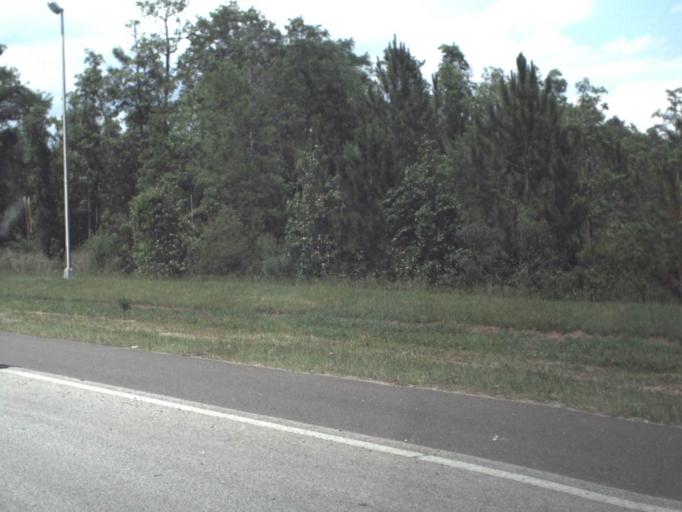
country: US
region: Florida
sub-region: Clay County
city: Bellair-Meadowbrook Terrace
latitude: 30.2031
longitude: -81.8373
